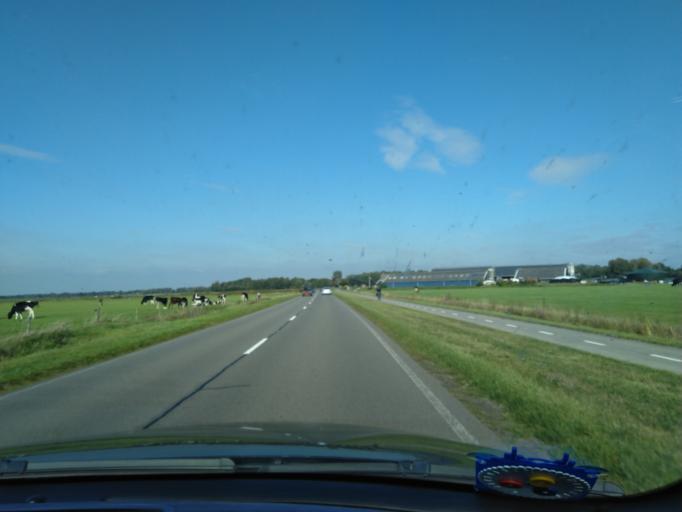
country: NL
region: Drenthe
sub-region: Gemeente Aa en Hunze
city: Anloo
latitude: 53.0684
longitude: 6.7593
